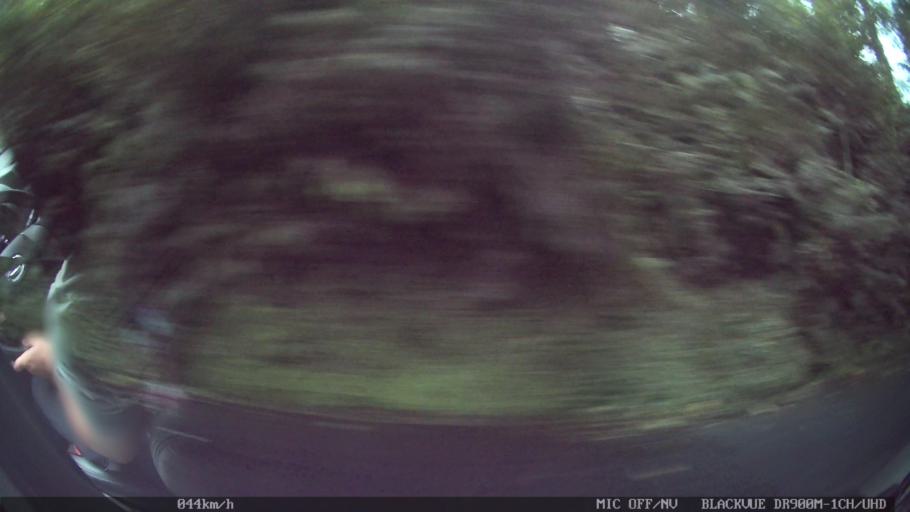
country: ID
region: Bali
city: Peneng
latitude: -8.3639
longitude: 115.1790
